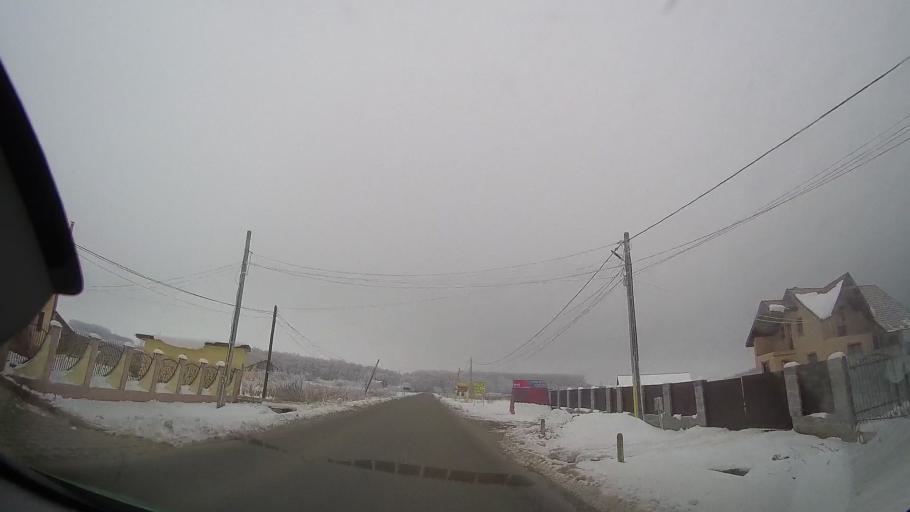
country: RO
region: Neamt
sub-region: Comuna Horia
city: Cotu Vames
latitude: 46.8769
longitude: 26.9759
